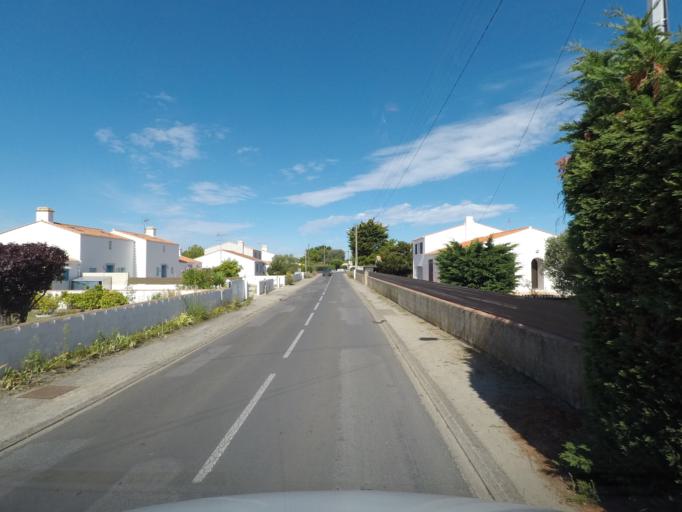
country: FR
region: Pays de la Loire
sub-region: Departement de la Vendee
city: La Gueriniere
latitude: 47.0012
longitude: -2.2269
